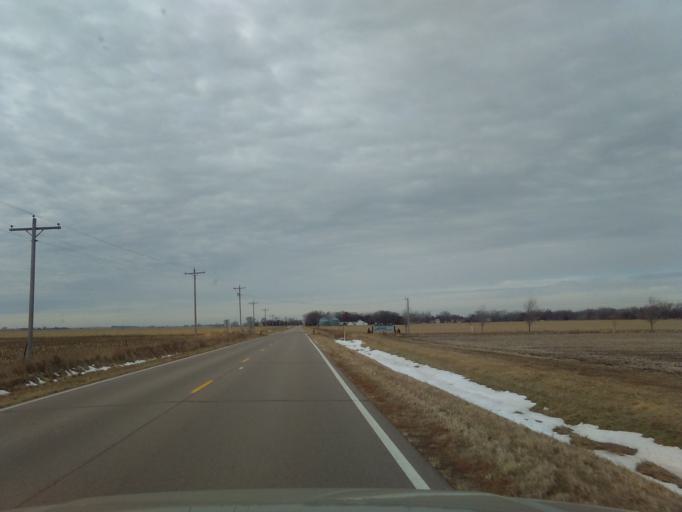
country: US
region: Nebraska
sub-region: Hall County
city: Grand Island
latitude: 40.7709
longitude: -98.4006
